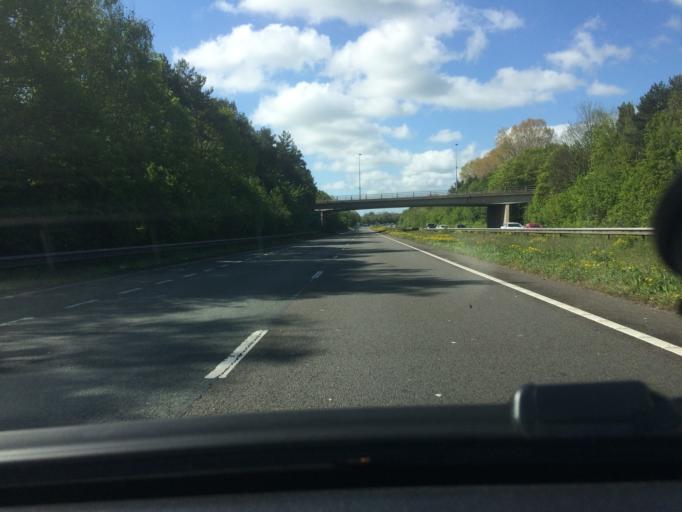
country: GB
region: England
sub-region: Cheshire West and Chester
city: Hoole
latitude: 53.1737
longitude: -2.8610
